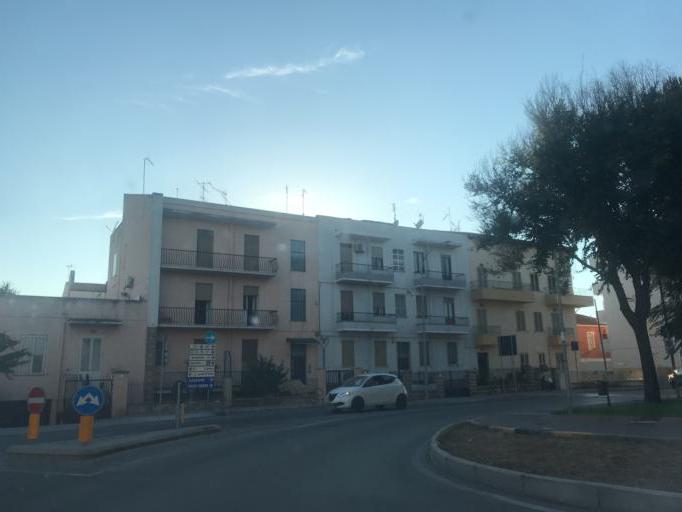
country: IT
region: Sardinia
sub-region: Provincia di Sassari
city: Alghero
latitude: 40.5729
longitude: 8.3225
